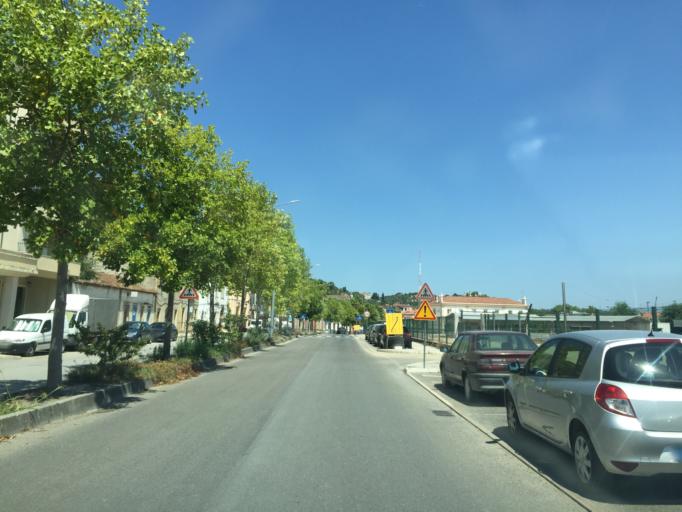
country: PT
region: Santarem
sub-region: Tomar
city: Tomar
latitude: 39.5973
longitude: -8.4129
